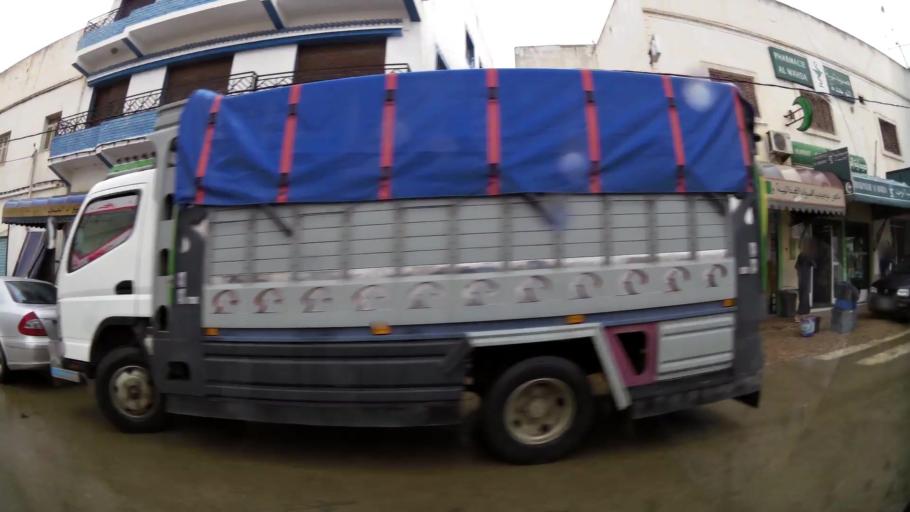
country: MA
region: Taza-Al Hoceima-Taounate
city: Imzourene
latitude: 35.1496
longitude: -3.8473
